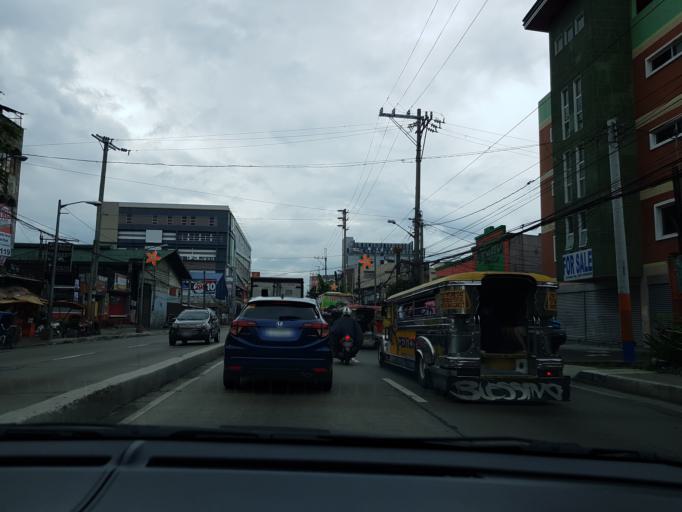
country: PH
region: Metro Manila
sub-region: Caloocan City
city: Niugan
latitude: 14.6612
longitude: 120.9841
